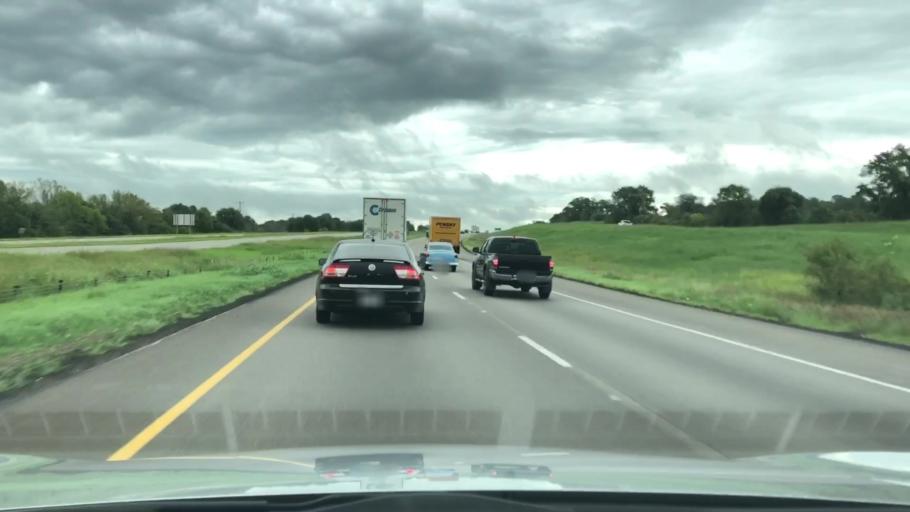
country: US
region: Texas
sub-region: Caldwell County
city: Luling
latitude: 29.6540
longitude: -97.5814
